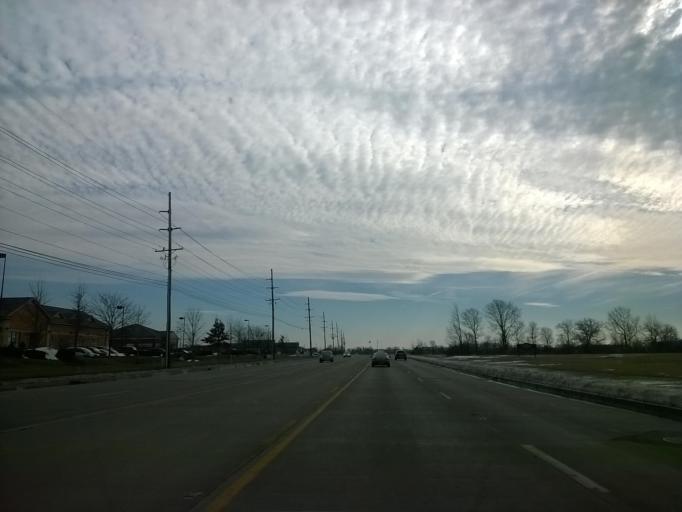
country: US
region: Indiana
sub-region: Boone County
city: Zionsville
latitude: 39.9480
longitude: -86.2399
